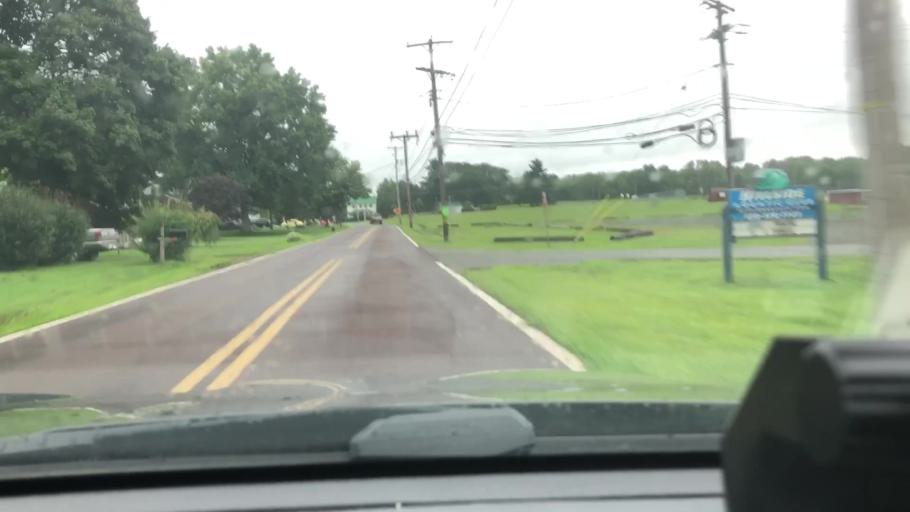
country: US
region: Pennsylvania
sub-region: Montgomery County
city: Halfway House
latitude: 40.2943
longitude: -75.6293
